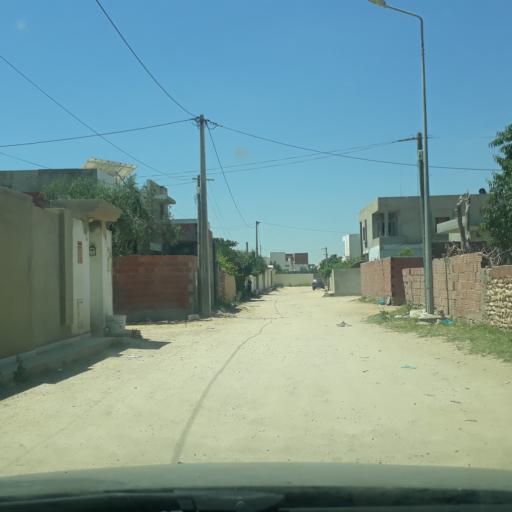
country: TN
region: Safaqis
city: Al Qarmadah
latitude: 34.8171
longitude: 10.7545
